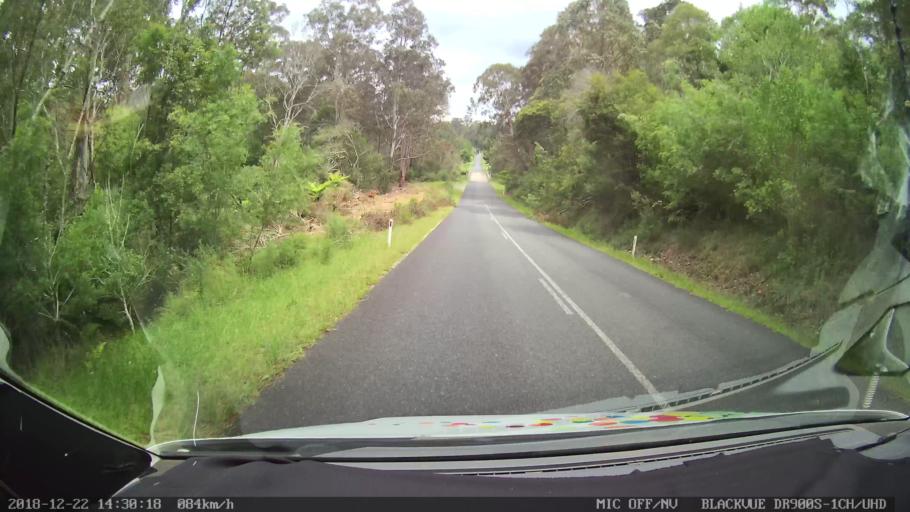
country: AU
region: New South Wales
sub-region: Bellingen
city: Dorrigo
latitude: -30.0846
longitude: 152.6318
